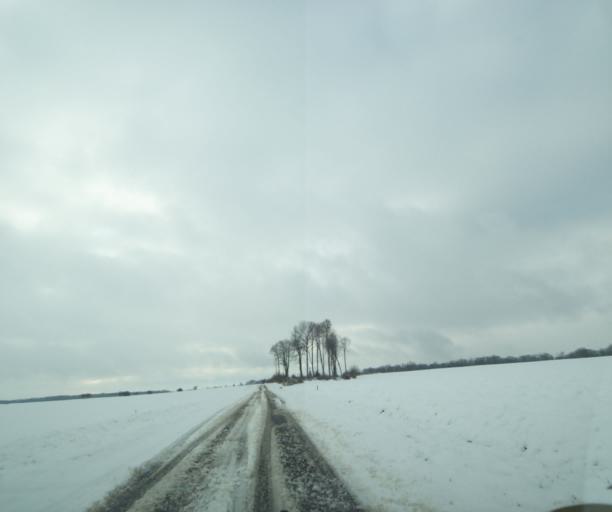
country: FR
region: Champagne-Ardenne
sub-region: Departement de la Haute-Marne
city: Montier-en-Der
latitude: 48.5031
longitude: 4.6863
